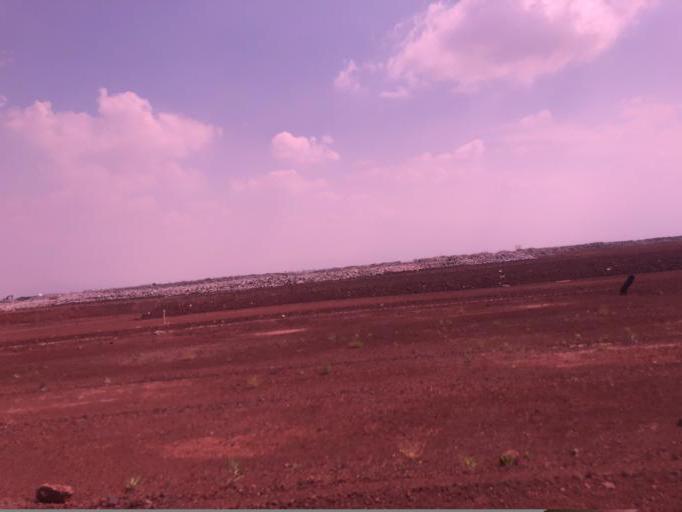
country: MX
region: Mexico
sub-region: Atenco
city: Colonia el Salado
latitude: 19.5336
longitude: -98.9942
